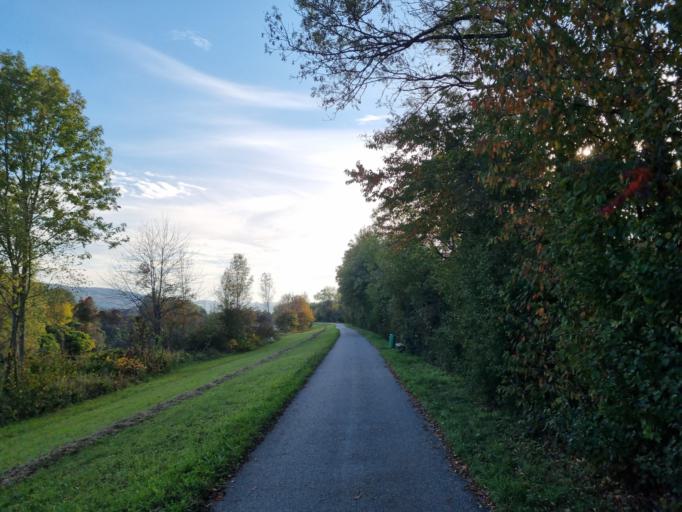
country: AT
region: Lower Austria
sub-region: Politischer Bezirk Sankt Polten
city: Wilhelmsburg
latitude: 48.1387
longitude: 15.6353
